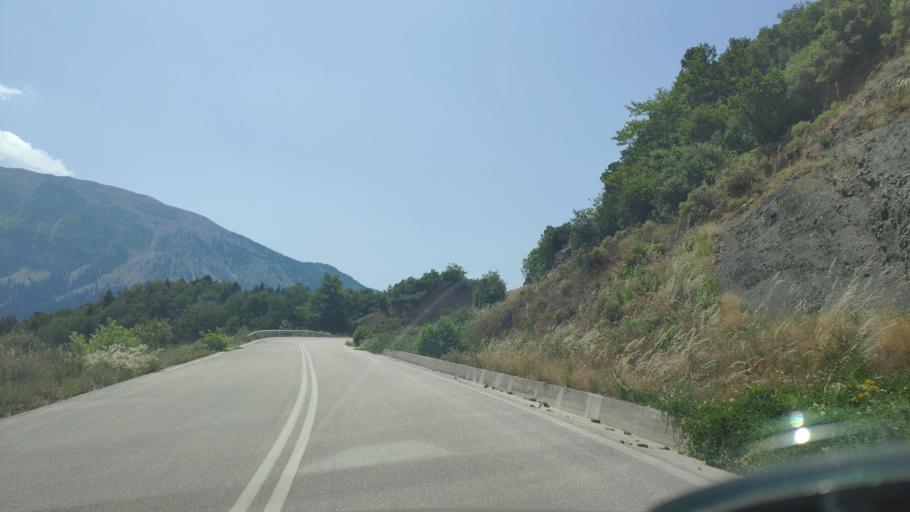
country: GR
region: Thessaly
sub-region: Nomos Kardhitsas
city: Anthiro
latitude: 39.2706
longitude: 21.3319
